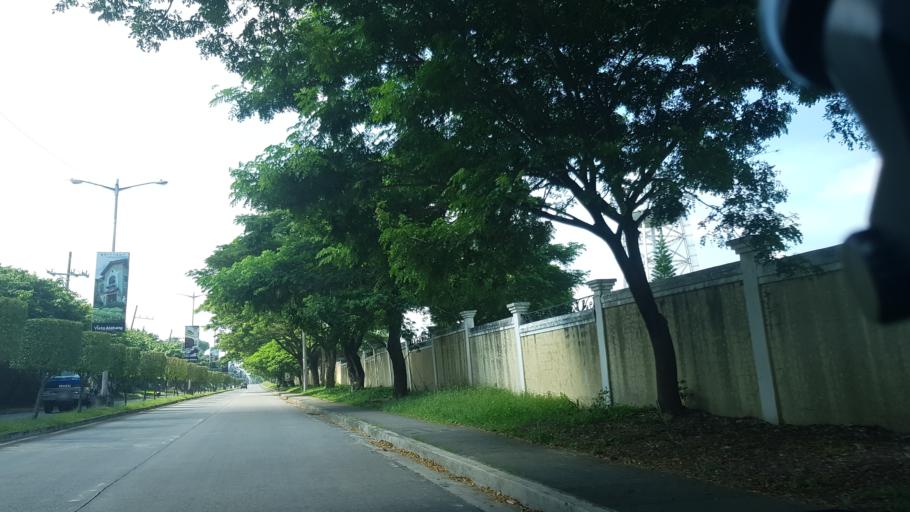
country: PH
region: Calabarzon
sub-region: Province of Laguna
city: Magsaysay
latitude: 14.3672
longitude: 121.0099
